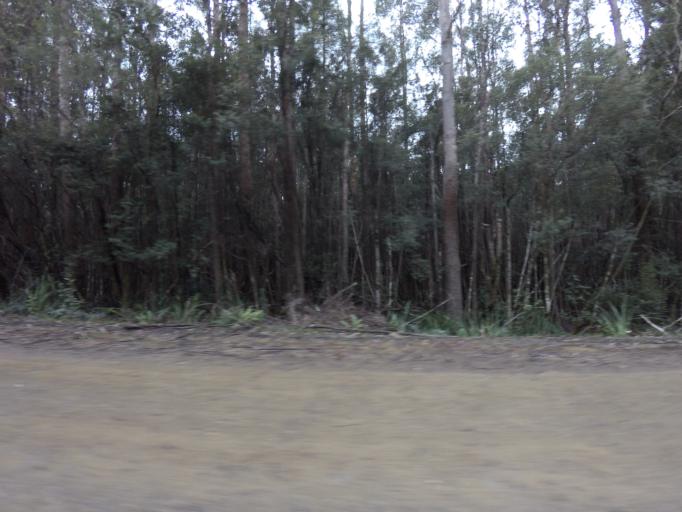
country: AU
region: Tasmania
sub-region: Huon Valley
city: Geeveston
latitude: -43.5252
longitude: 146.8829
